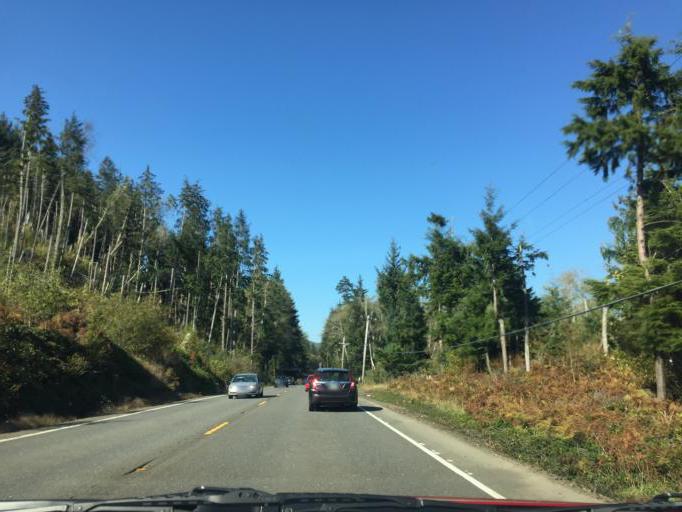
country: US
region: Oregon
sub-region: Clatsop County
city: Cannon Beach
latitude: 45.9033
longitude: -123.8730
